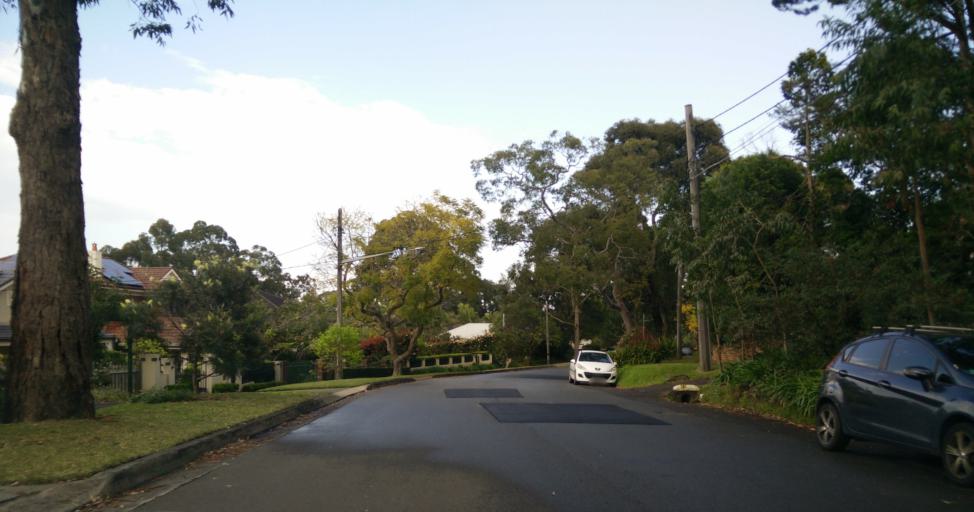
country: AU
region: New South Wales
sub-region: Ku-ring-gai
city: Killara
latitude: -33.7755
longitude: 151.1588
